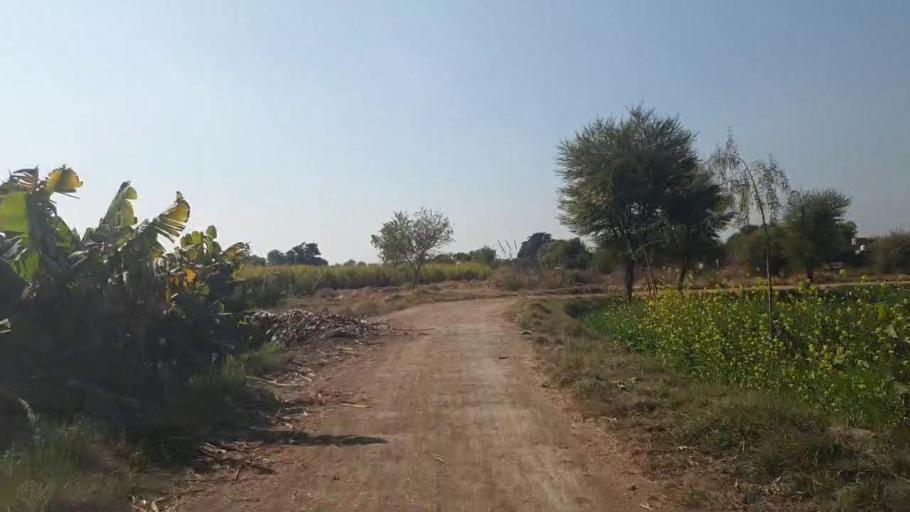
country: PK
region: Sindh
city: Shahdadpur
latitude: 25.9257
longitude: 68.5726
